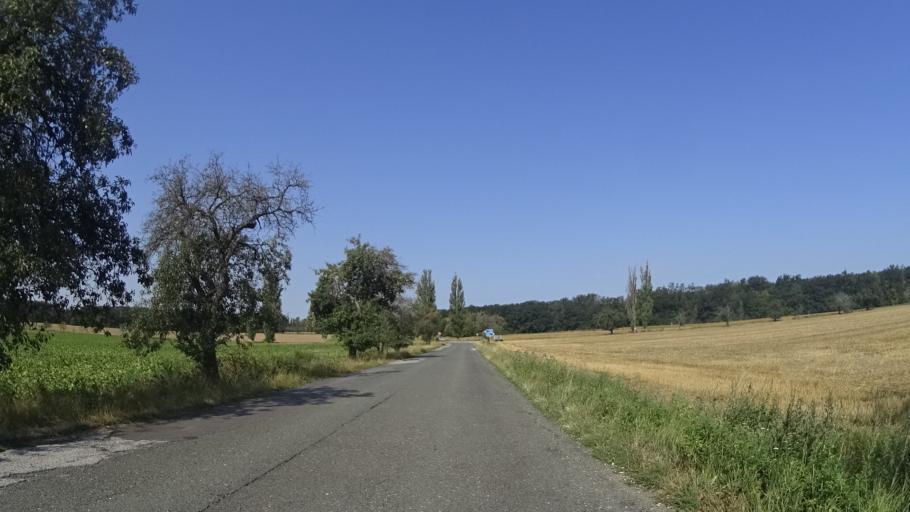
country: CZ
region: Kralovehradecky
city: Novy Bydzov
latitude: 50.2791
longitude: 15.5432
